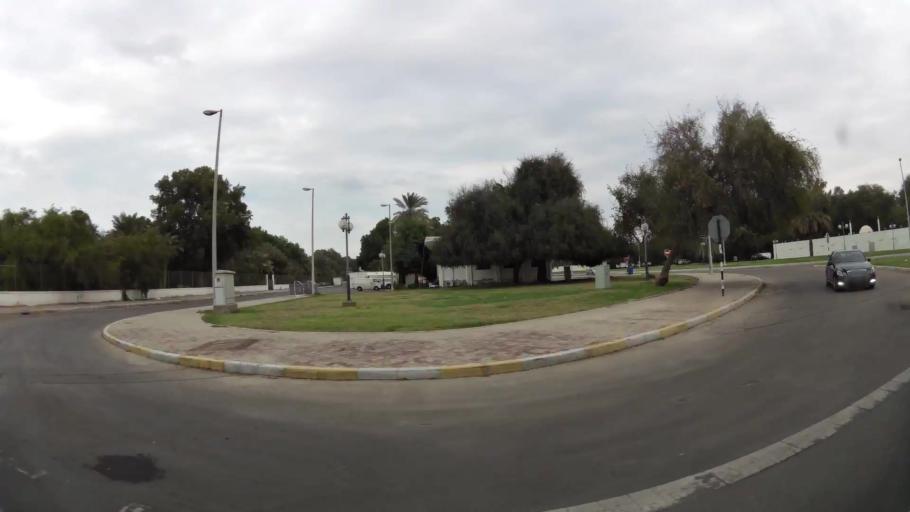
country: AE
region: Abu Dhabi
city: Abu Dhabi
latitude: 24.4278
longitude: 54.3789
